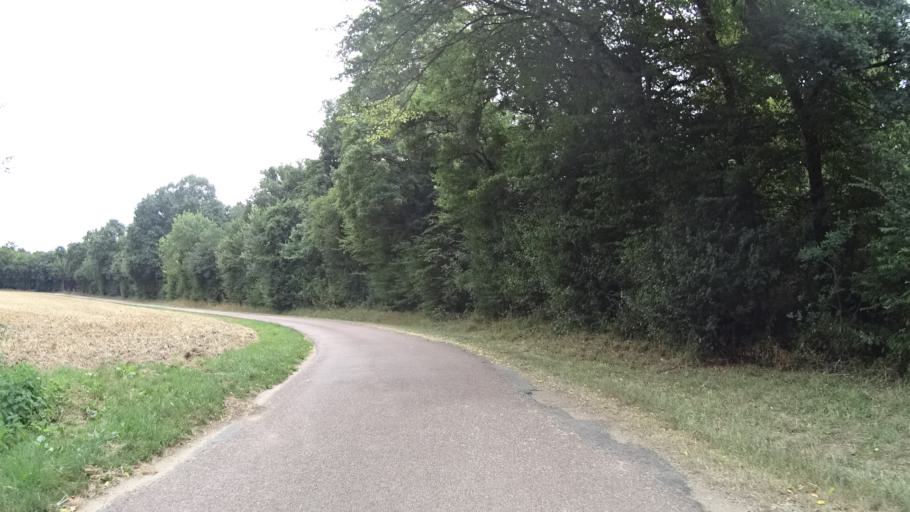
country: FR
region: Centre
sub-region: Departement du Loiret
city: Saint-Germain-des-Pres
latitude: 47.9461
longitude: 2.8107
